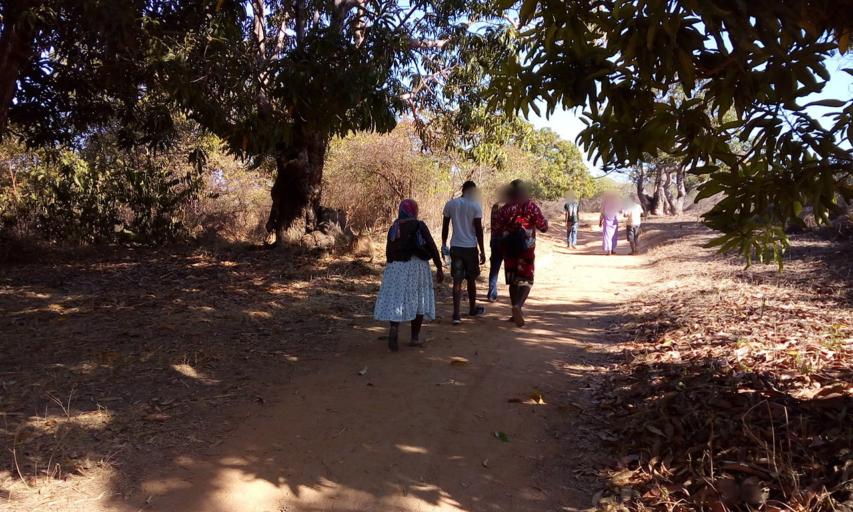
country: MG
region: Boeny
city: Mahajanga
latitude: -15.6270
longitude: 46.4208
